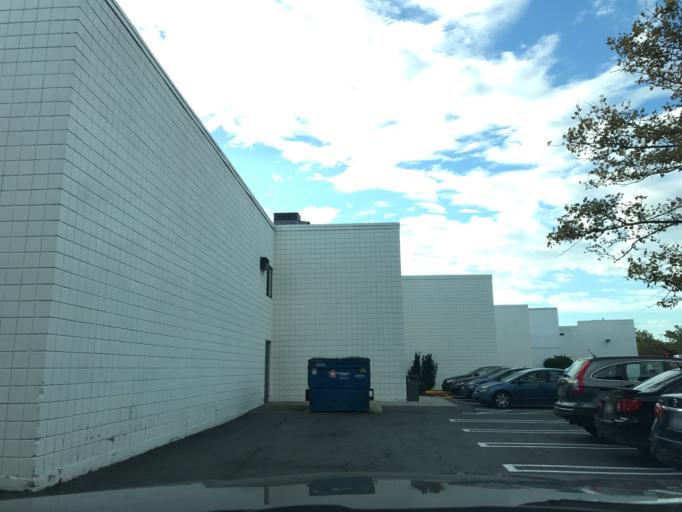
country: US
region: Massachusetts
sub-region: Middlesex County
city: Watertown
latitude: 42.3647
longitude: -71.1589
